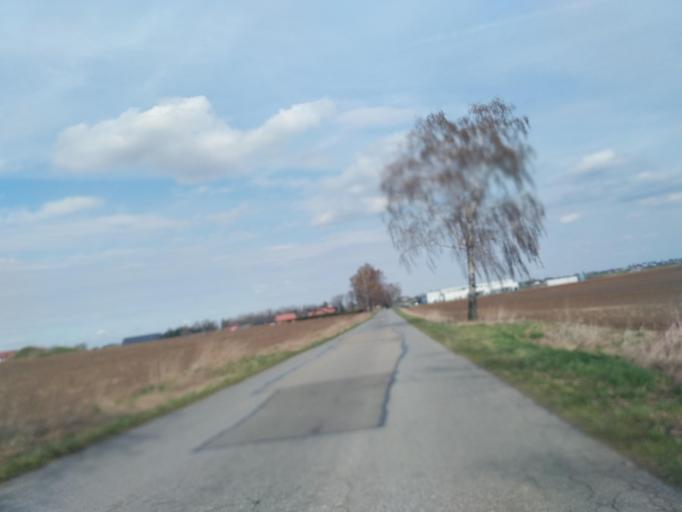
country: PL
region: Subcarpathian Voivodeship
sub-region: Powiat ropczycko-sedziszowski
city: Sedziszow Malopolski
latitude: 50.0551
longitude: 21.7141
